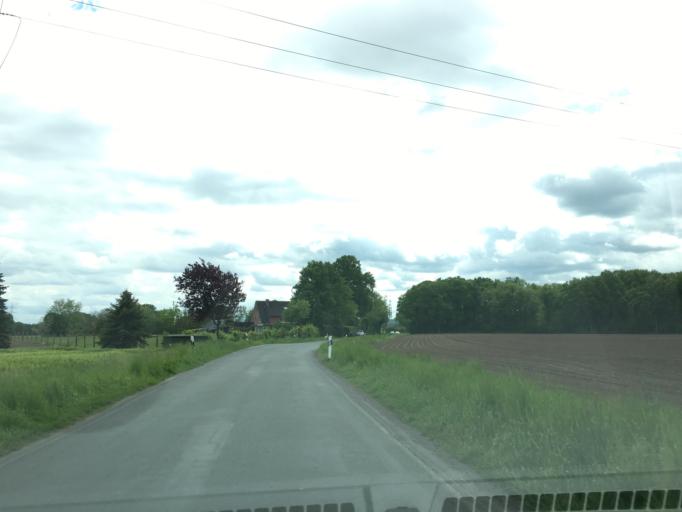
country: DE
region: North Rhine-Westphalia
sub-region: Regierungsbezirk Munster
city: Havixbeck
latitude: 51.9760
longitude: 7.4690
